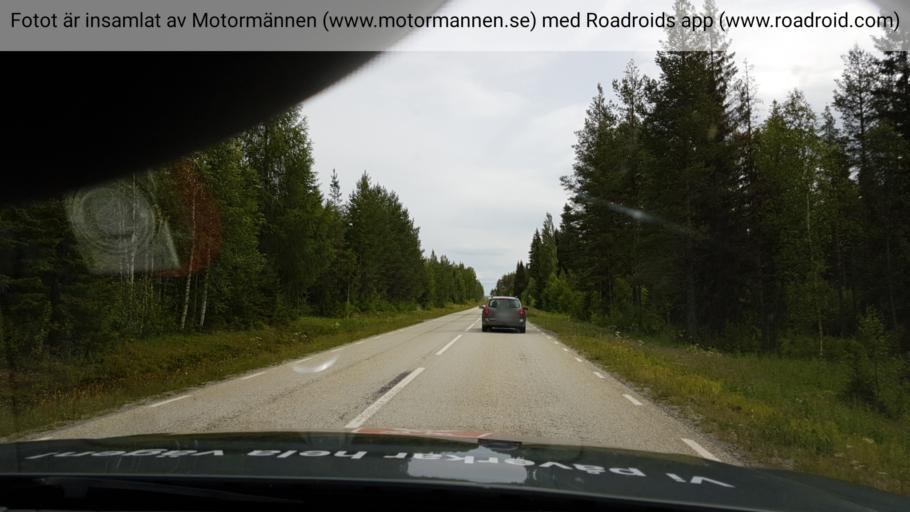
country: SE
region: Jaemtland
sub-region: Bergs Kommun
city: Hoverberg
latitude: 62.6551
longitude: 14.3256
